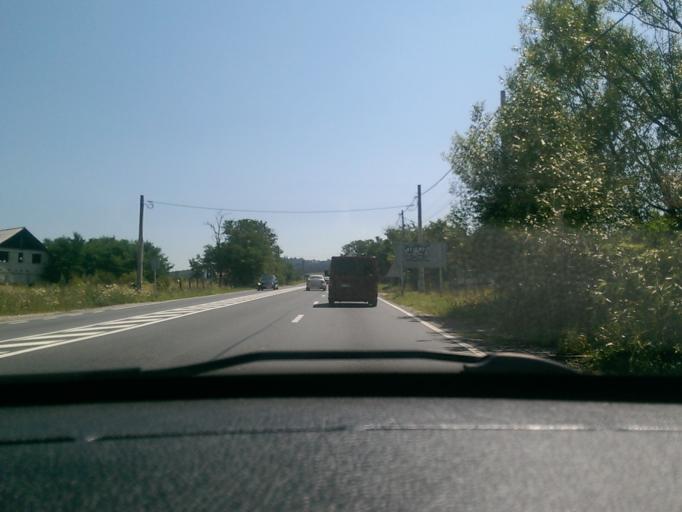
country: RO
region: Cluj
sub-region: Comuna Feleacu
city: Feleacu
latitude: 46.7310
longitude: 23.5972
